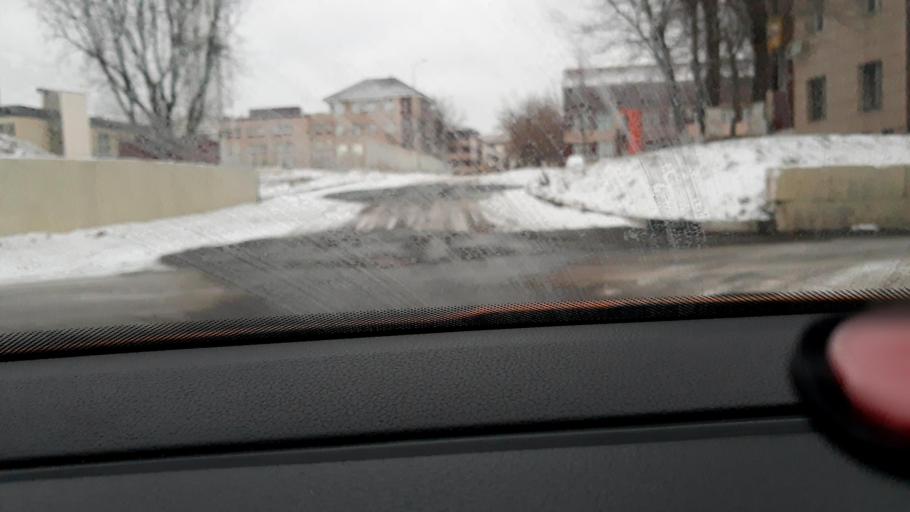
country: RU
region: Moskovskaya
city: Kozhukhovo
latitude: 55.7104
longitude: 37.6905
